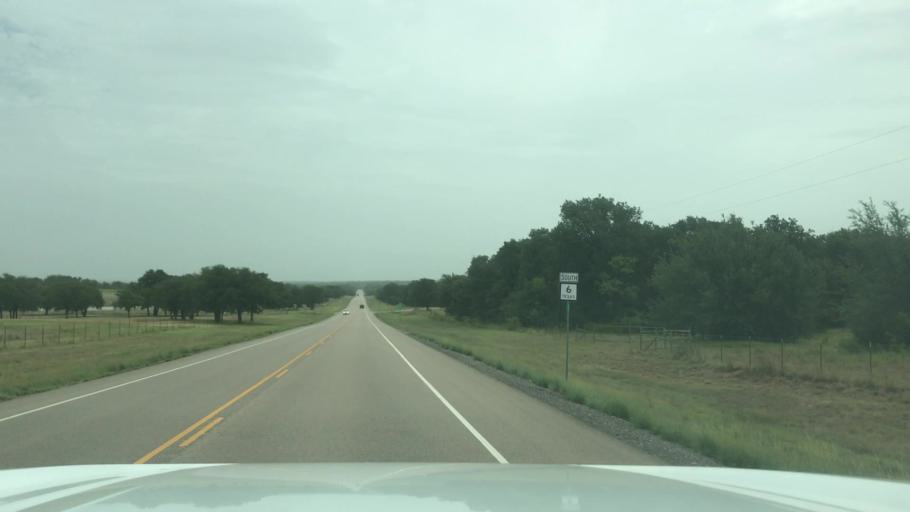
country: US
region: Texas
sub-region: Hamilton County
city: Hico
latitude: 31.9782
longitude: -97.9138
